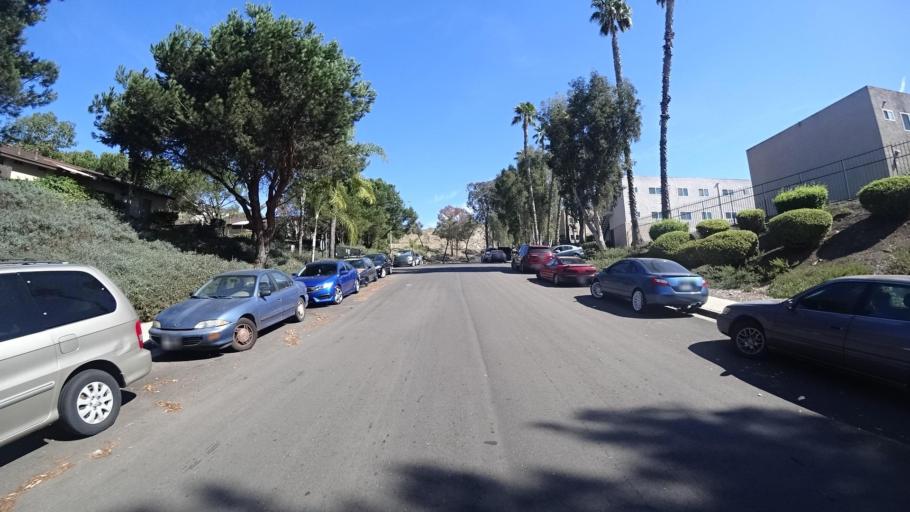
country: US
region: California
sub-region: San Diego County
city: La Presa
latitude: 32.7205
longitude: -117.0009
